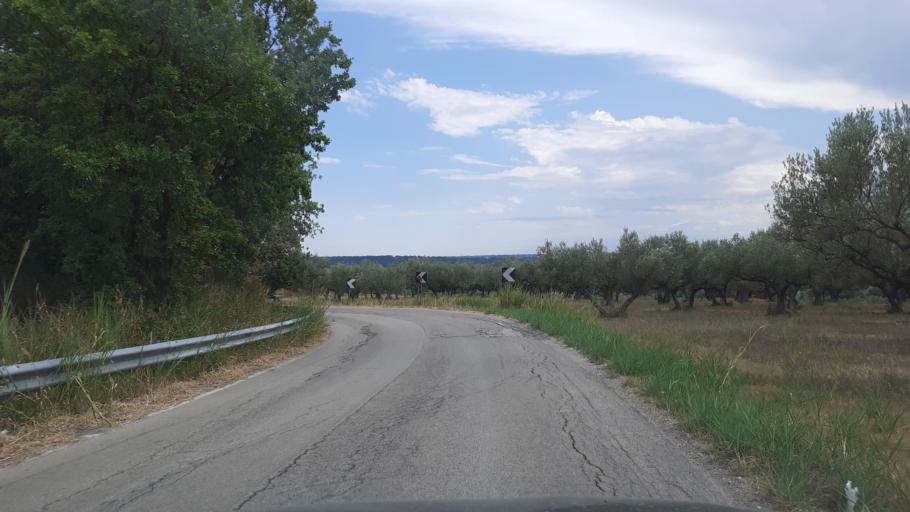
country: IT
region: Abruzzo
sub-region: Provincia di Chieti
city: Fossacesia
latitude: 42.2551
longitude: 14.5017
